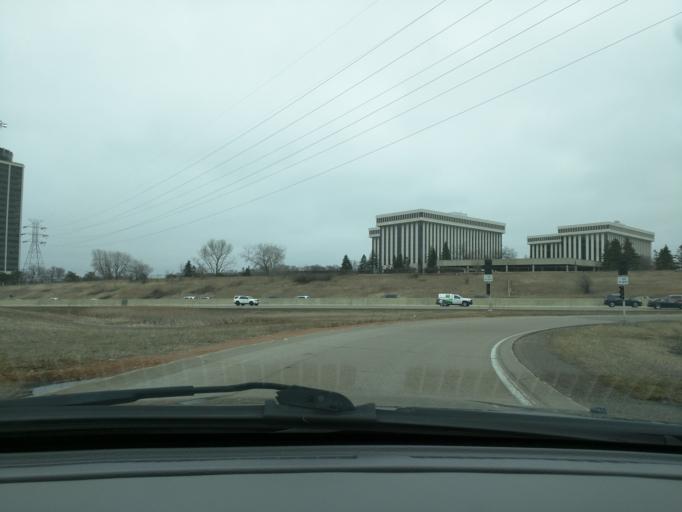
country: US
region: Minnesota
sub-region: Hennepin County
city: Bloomington
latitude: 44.8604
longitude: -93.3274
